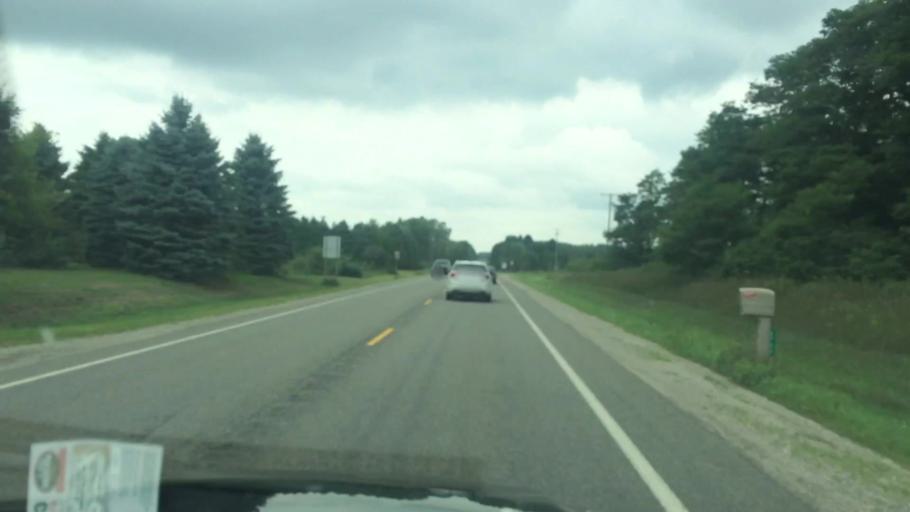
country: US
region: Michigan
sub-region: Tuscola County
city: Cass City
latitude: 43.6162
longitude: -83.0969
